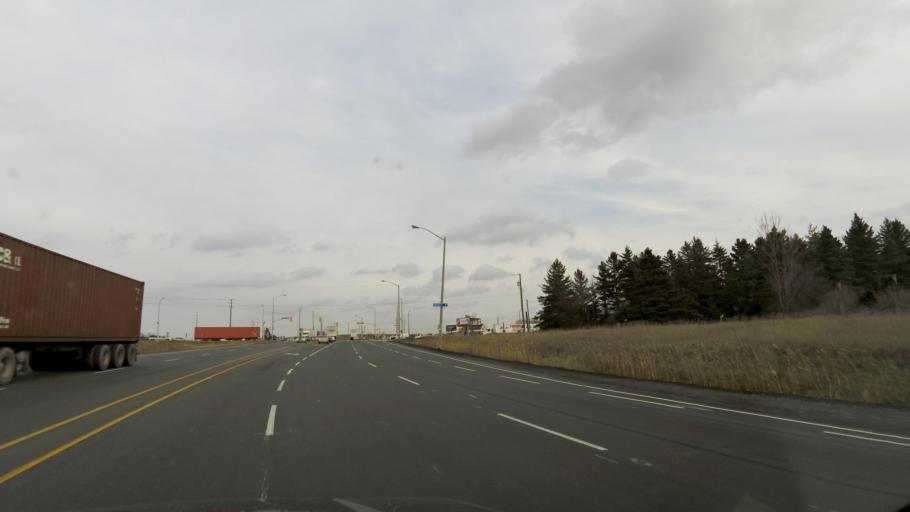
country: CA
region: Ontario
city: Etobicoke
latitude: 43.7490
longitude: -79.6408
